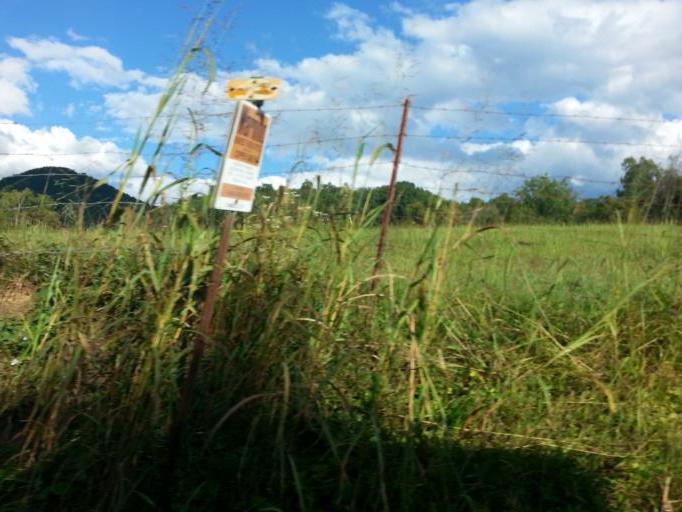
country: US
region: Tennessee
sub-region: Knox County
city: Mascot
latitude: 36.1033
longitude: -83.7866
